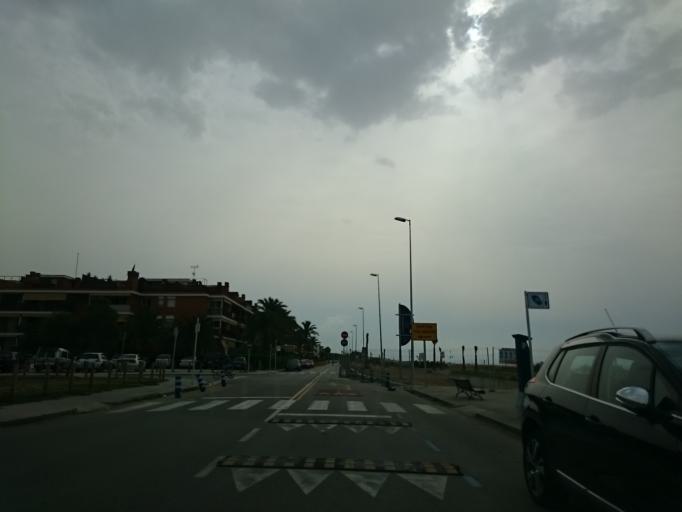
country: ES
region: Catalonia
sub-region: Provincia de Barcelona
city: Castelldefels
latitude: 41.2645
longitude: 1.9440
